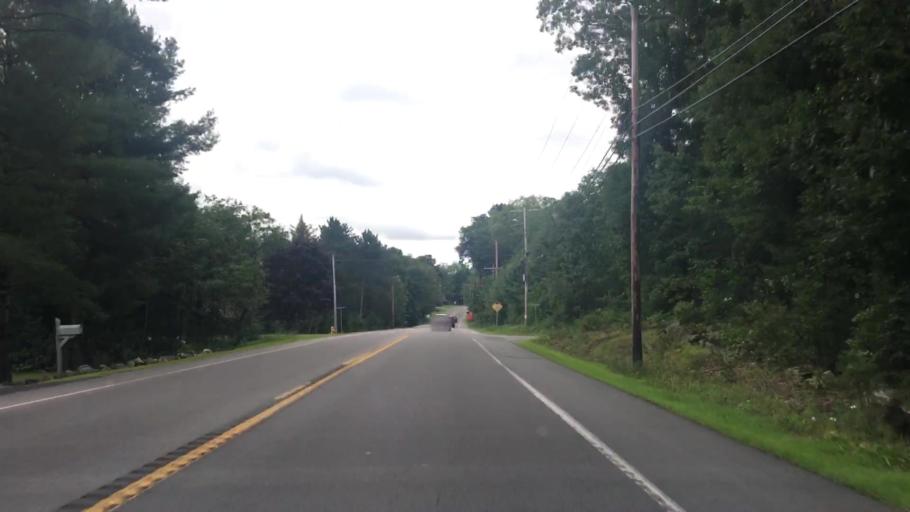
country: US
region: Maine
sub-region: York County
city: Alfred
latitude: 43.4825
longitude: -70.7181
